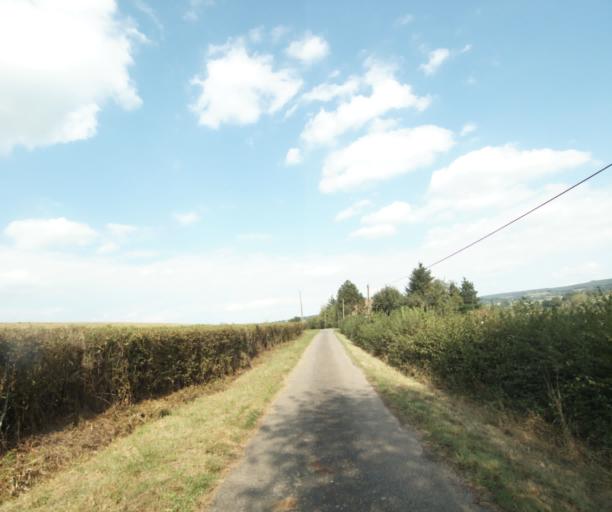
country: FR
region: Bourgogne
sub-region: Departement de Saone-et-Loire
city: Palinges
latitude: 46.4899
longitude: 4.2249
